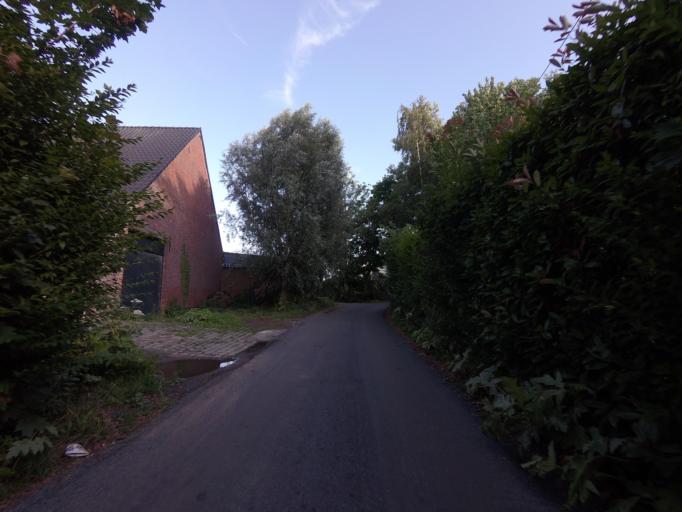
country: BE
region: Flanders
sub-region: Provincie Antwerpen
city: Edegem
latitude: 51.1481
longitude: 4.4392
